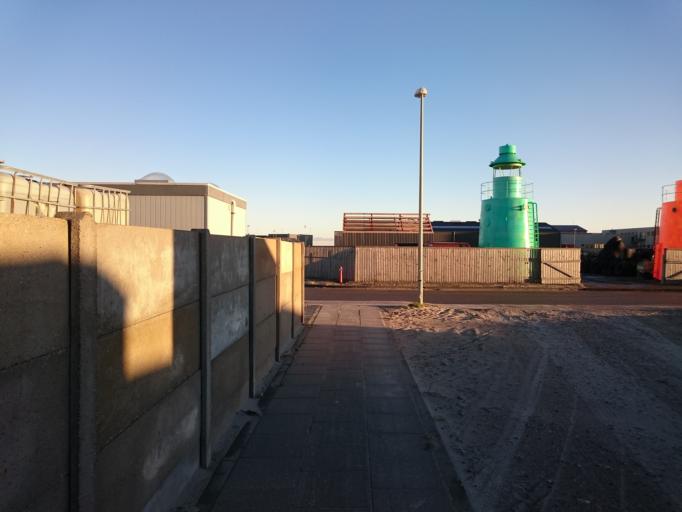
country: DK
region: North Denmark
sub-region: Frederikshavn Kommune
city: Skagen
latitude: 57.7151
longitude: 10.5792
